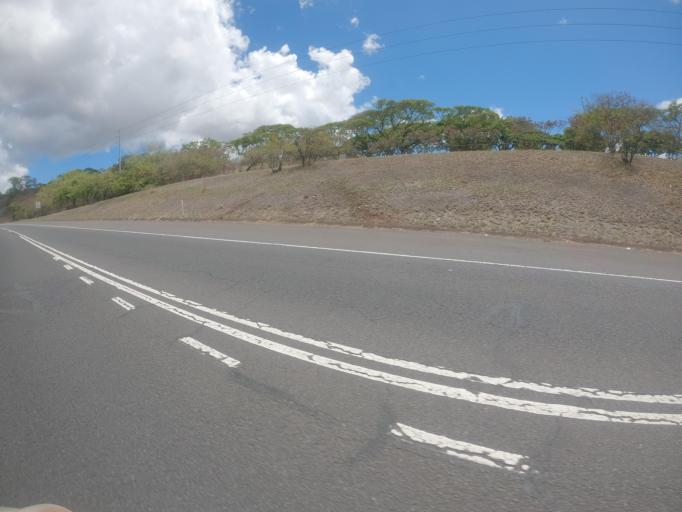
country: US
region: Hawaii
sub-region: Honolulu County
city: Halawa Heights
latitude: 21.3686
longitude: -157.9103
